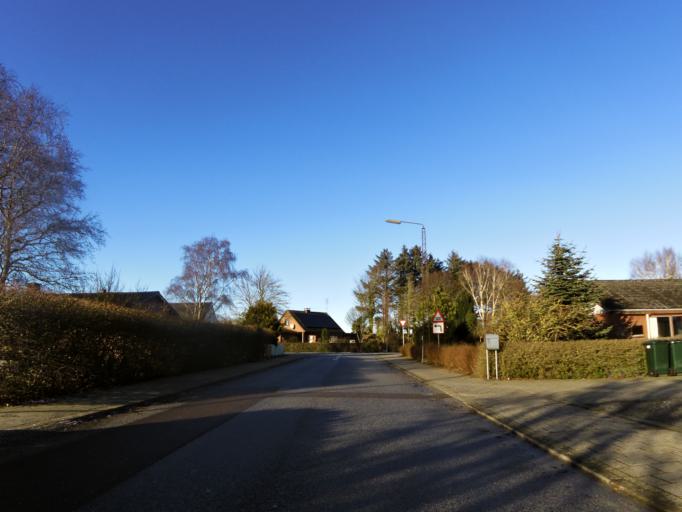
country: DK
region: South Denmark
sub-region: Tonder Kommune
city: Sherrebek
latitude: 55.1631
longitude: 8.7692
